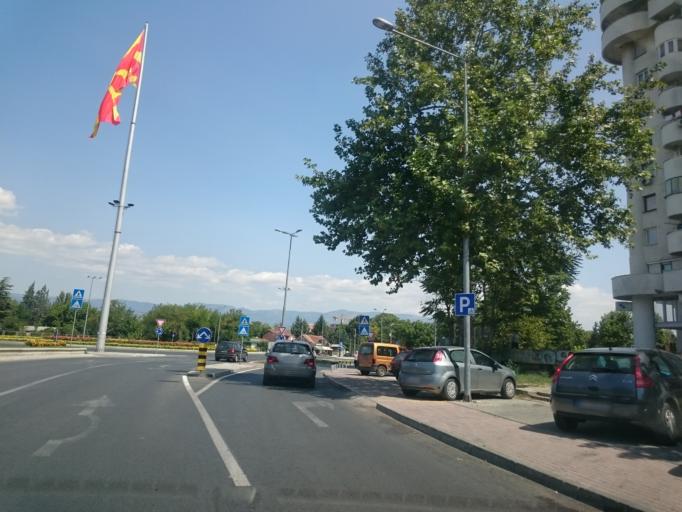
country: MK
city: Krushopek
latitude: 42.0079
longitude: 21.3681
